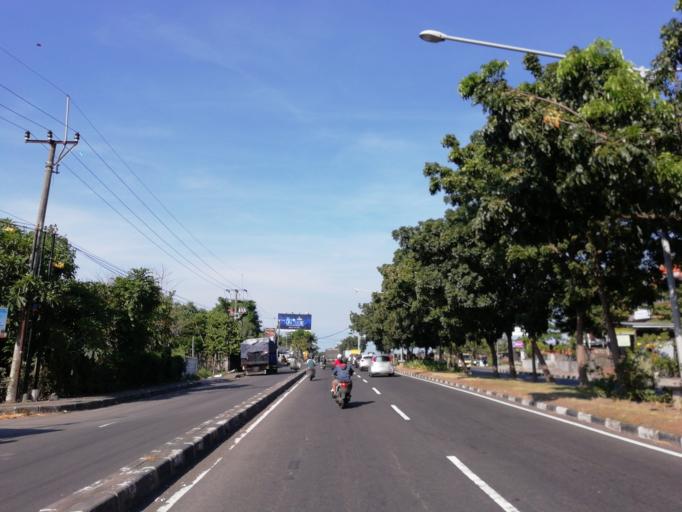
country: ID
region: Bali
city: Banjar Kertajiwa
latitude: -8.6485
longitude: 115.2681
